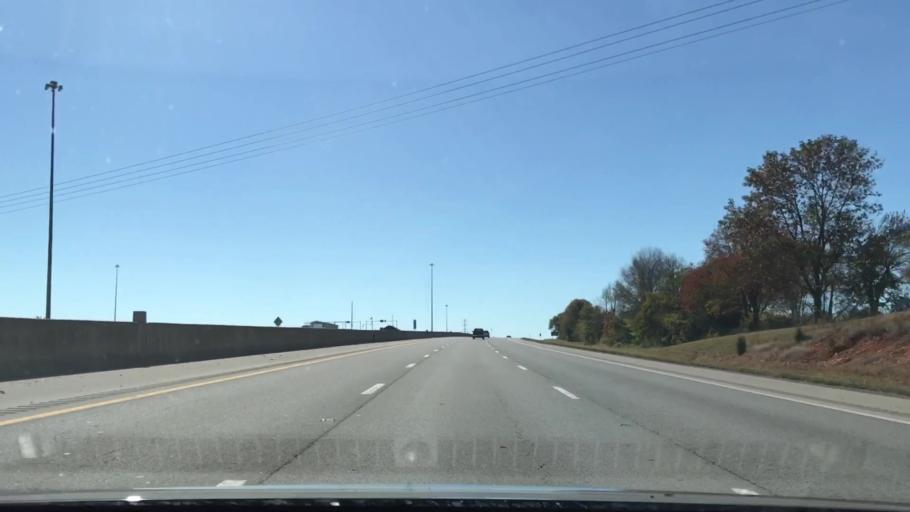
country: US
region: Kentucky
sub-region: Simpson County
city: Franklin
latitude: 36.6902
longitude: -86.5362
